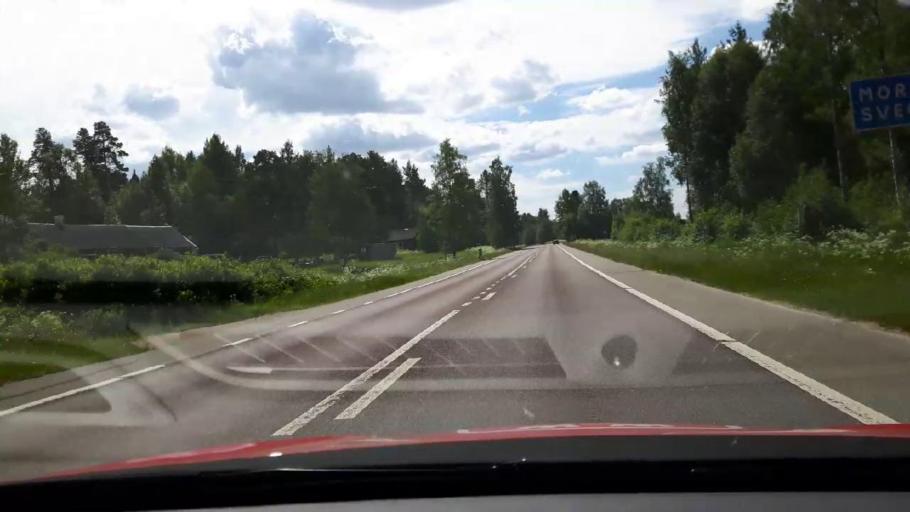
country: SE
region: Jaemtland
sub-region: Harjedalens Kommun
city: Sveg
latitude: 62.1695
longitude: 14.9512
